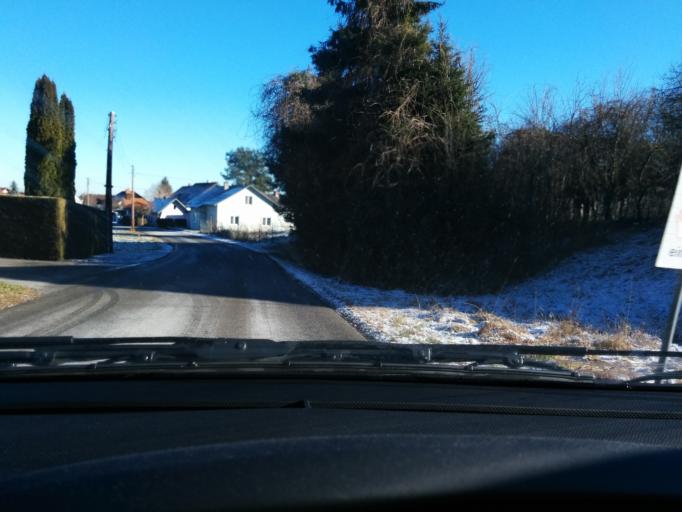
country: AT
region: Styria
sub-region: Politischer Bezirk Weiz
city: Nitscha
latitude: 47.1212
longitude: 15.7420
